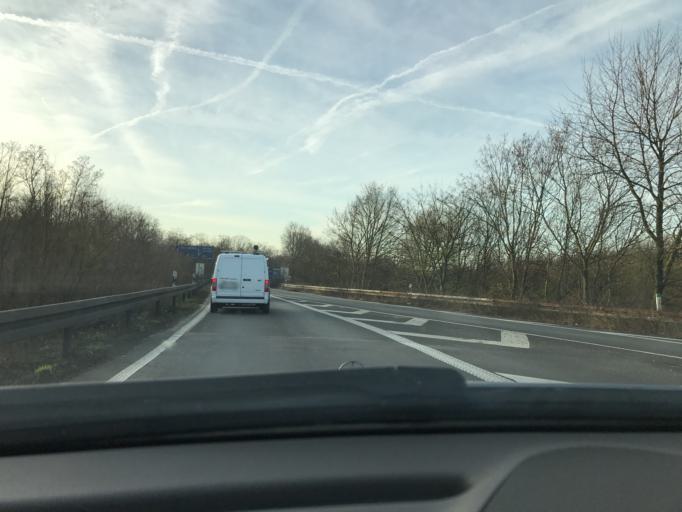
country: DE
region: North Rhine-Westphalia
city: Meiderich
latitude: 51.4862
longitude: 6.8123
